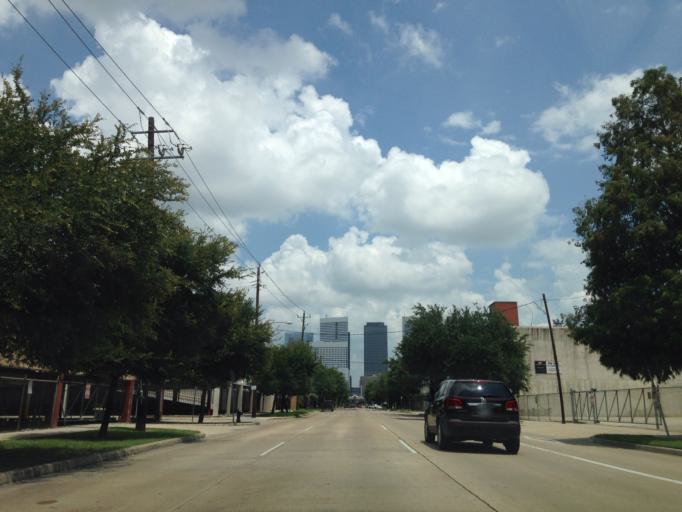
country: US
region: Texas
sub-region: Harris County
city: Houston
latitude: 29.7446
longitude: -95.3722
